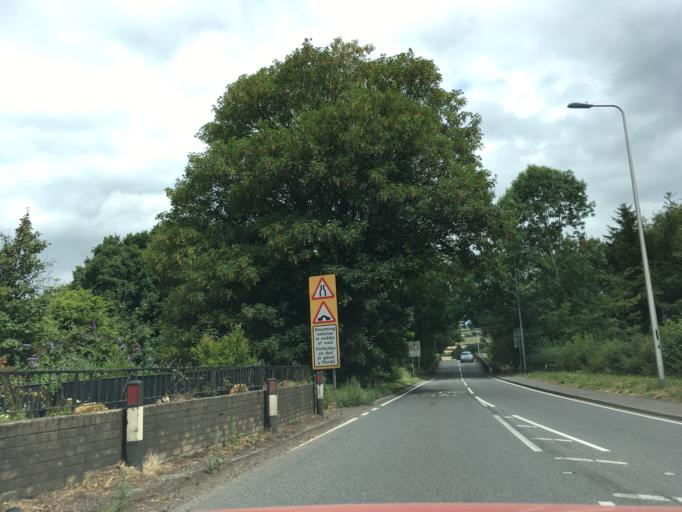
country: GB
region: Wales
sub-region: Monmouthshire
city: Abergavenny
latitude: 51.7926
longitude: -3.0094
